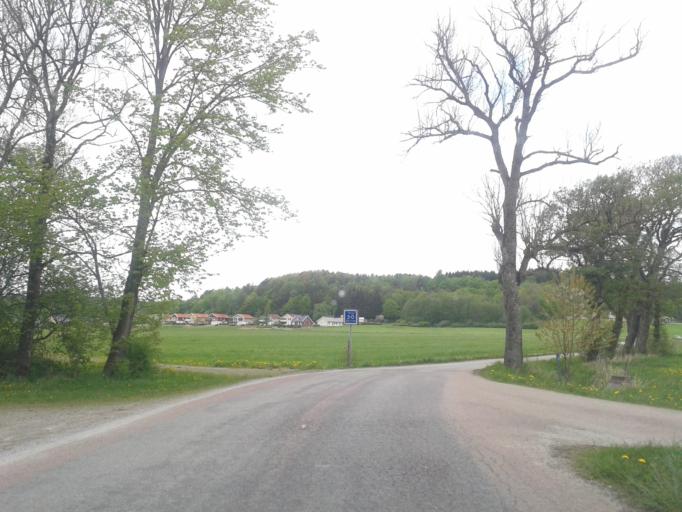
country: SE
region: Vaestra Goetaland
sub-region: Kungalvs Kommun
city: Kungalv
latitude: 57.8825
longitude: 12.0042
